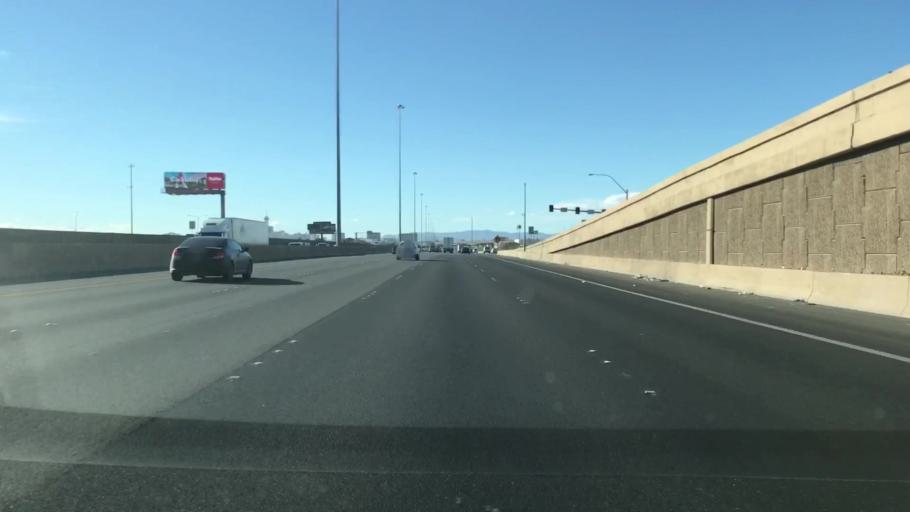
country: US
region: Nevada
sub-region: Clark County
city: North Las Vegas
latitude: 36.2158
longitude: -115.1261
